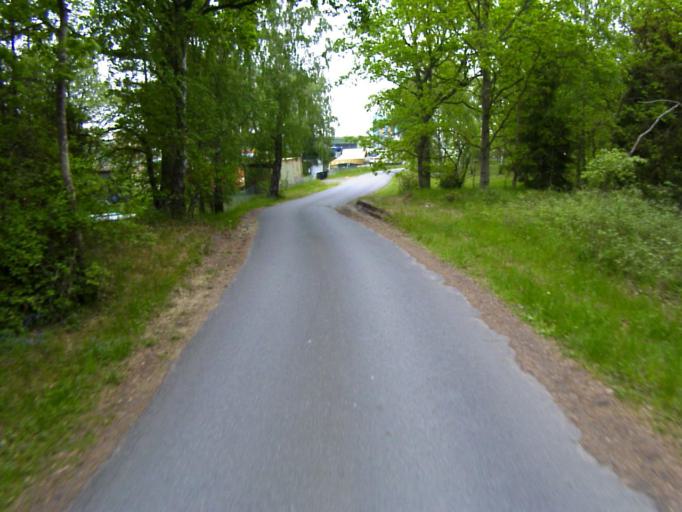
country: SE
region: Skane
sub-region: Kristianstads Kommun
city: Ahus
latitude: 55.9256
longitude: 14.3131
